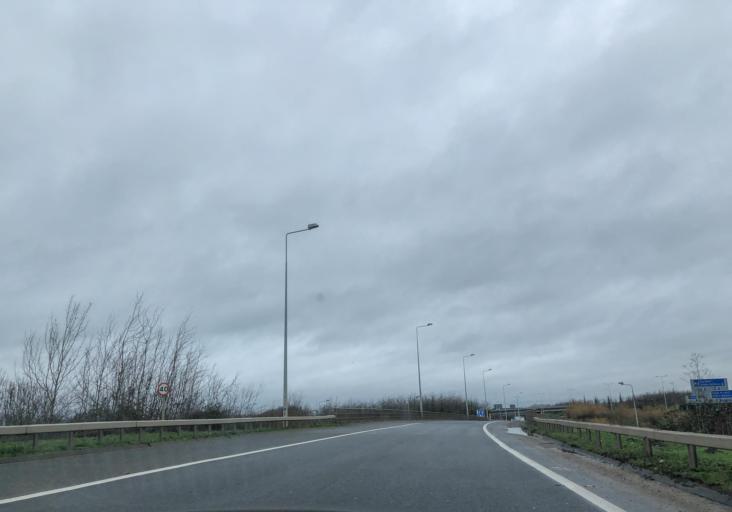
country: GB
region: England
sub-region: Surrey
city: Colnbrook
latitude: 51.4701
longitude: -0.5080
